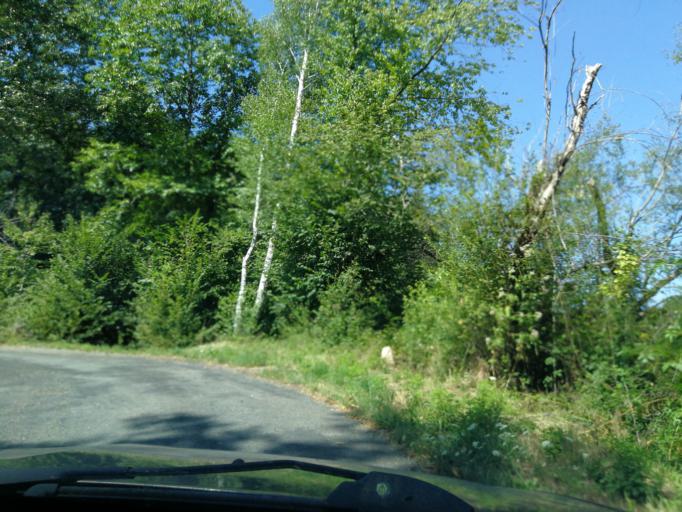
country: FR
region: Midi-Pyrenees
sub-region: Departement de l'Aveyron
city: Livinhac-le-Haut
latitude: 44.6824
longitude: 2.3278
